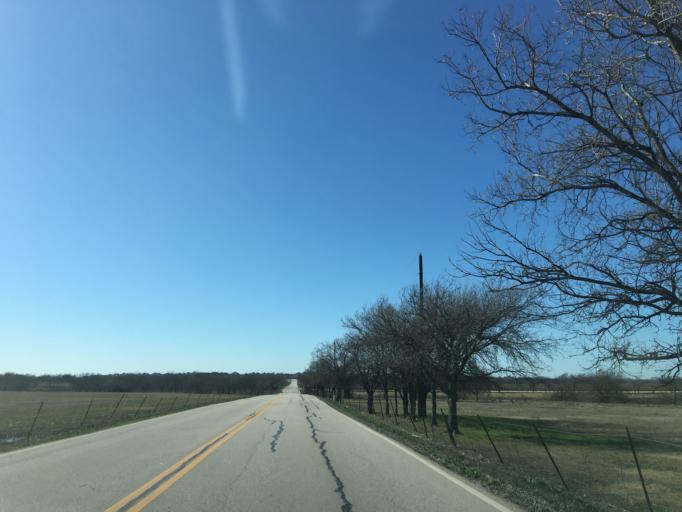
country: US
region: Texas
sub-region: Collin County
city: Prosper
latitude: 33.2330
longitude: -96.8357
